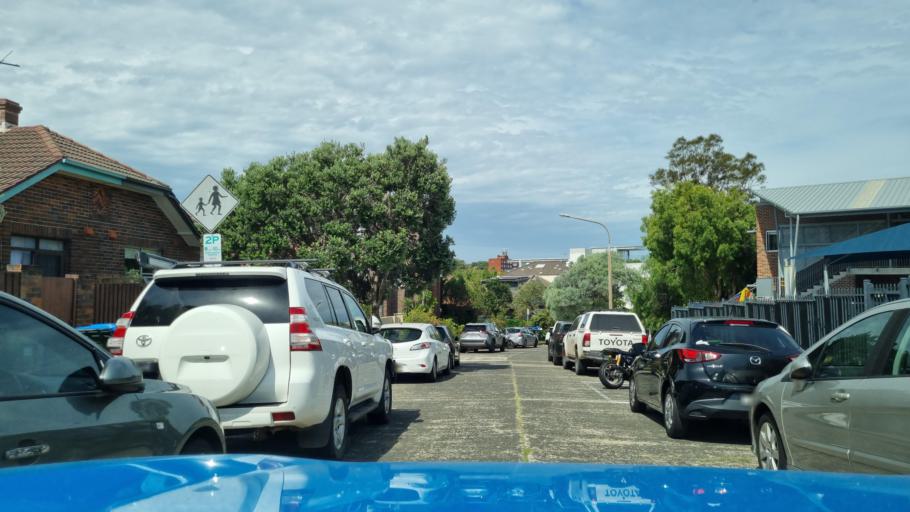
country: AU
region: New South Wales
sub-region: Waverley
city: North Bondi
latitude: -33.8862
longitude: 151.2786
